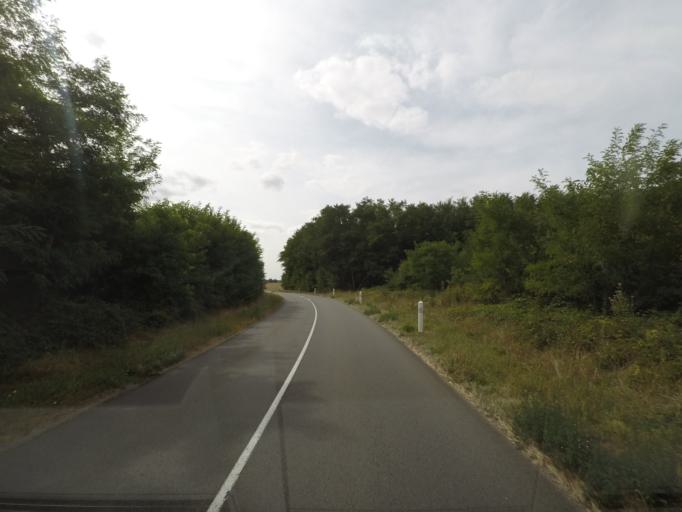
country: FR
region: Poitou-Charentes
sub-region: Departement de la Charente
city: Nanteuil-en-Vallee
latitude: 46.0186
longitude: 0.2922
